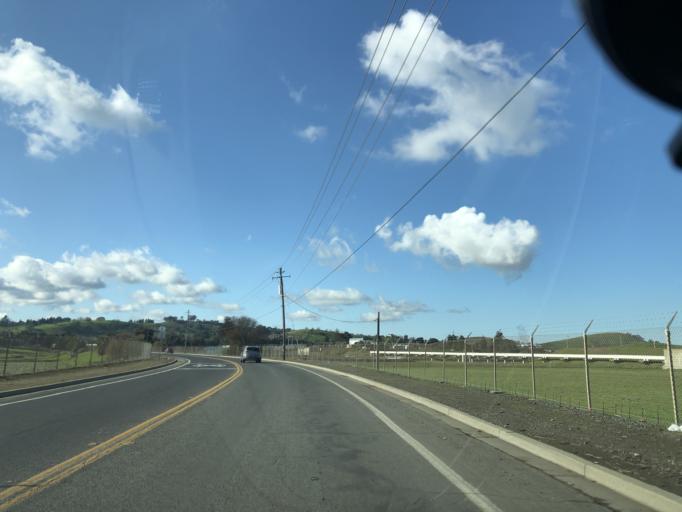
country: US
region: California
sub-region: Contra Costa County
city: Pacheco
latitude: 38.0019
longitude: -122.0635
